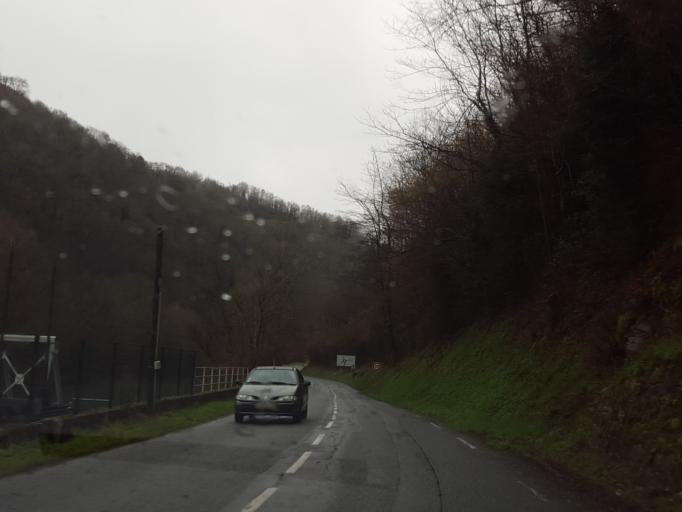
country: FR
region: Midi-Pyrenees
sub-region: Departement de l'Ariege
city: Saint-Girons
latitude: 42.9109
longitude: 1.2095
